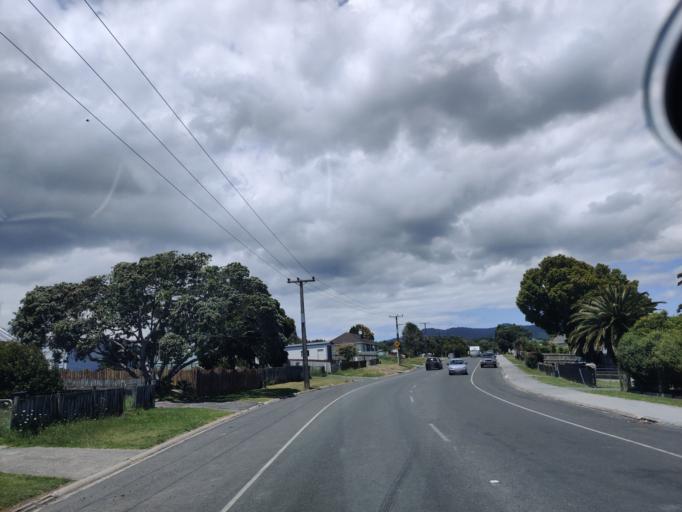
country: NZ
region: Northland
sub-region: Far North District
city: Kaitaia
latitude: -35.1170
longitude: 173.2579
